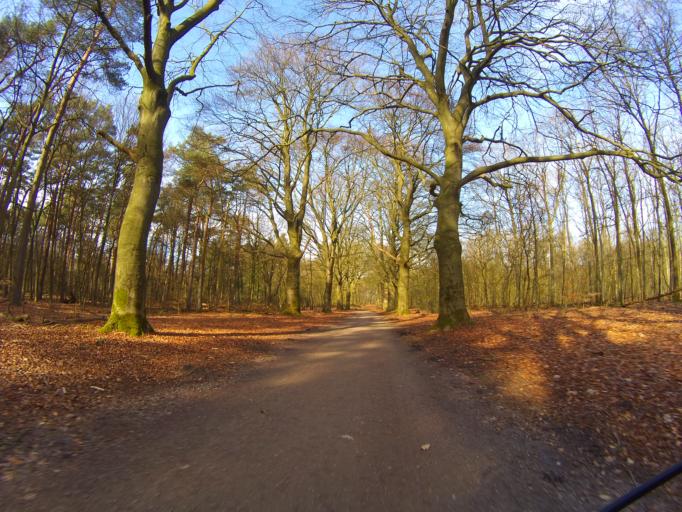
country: NL
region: North Holland
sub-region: Gemeente Bussum
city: Bussum
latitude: 52.2576
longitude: 5.1589
